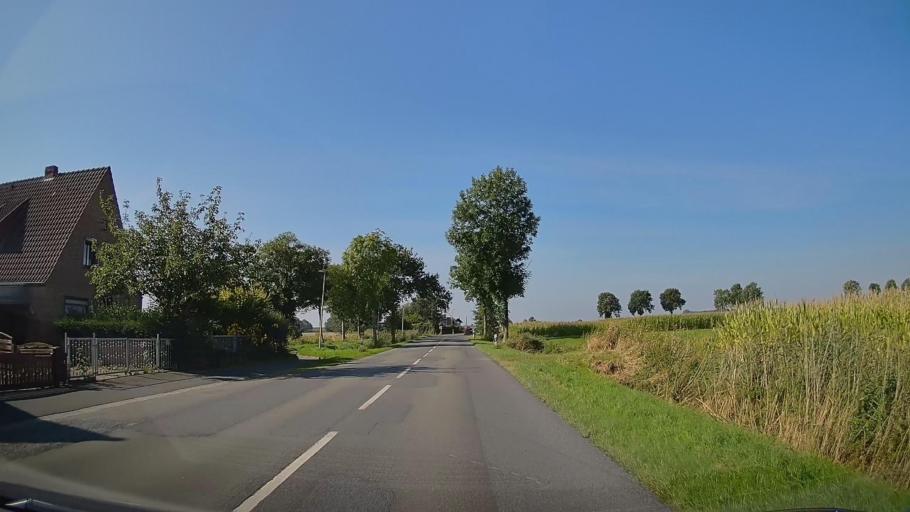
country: DE
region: Lower Saxony
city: Wremen
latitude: 53.6148
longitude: 8.5282
